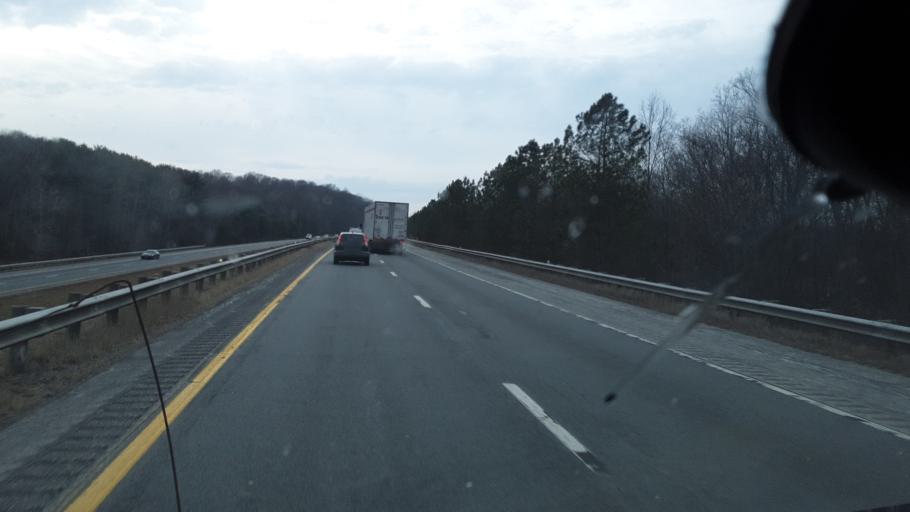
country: US
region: Ohio
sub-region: Summit County
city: Montrose-Ghent
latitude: 41.1979
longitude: -81.6966
